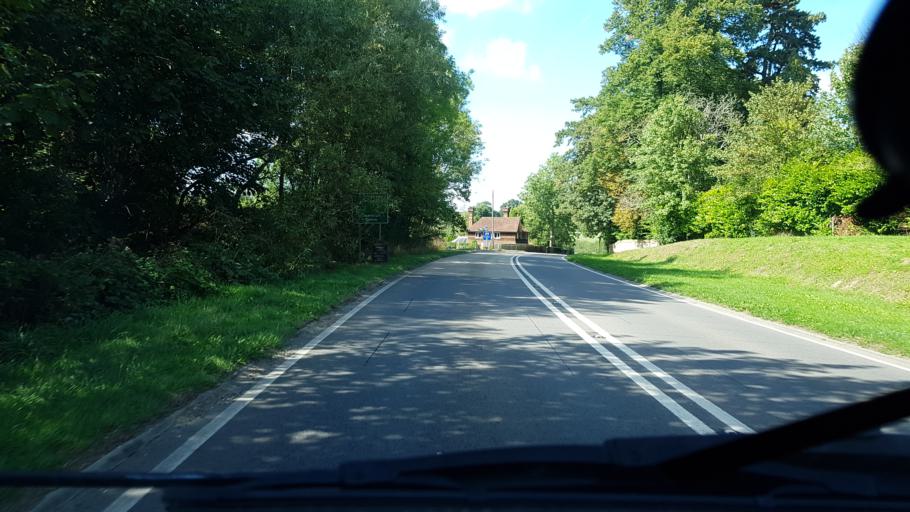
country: GB
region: England
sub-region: West Sussex
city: Horsham
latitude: 51.0907
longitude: -0.3394
